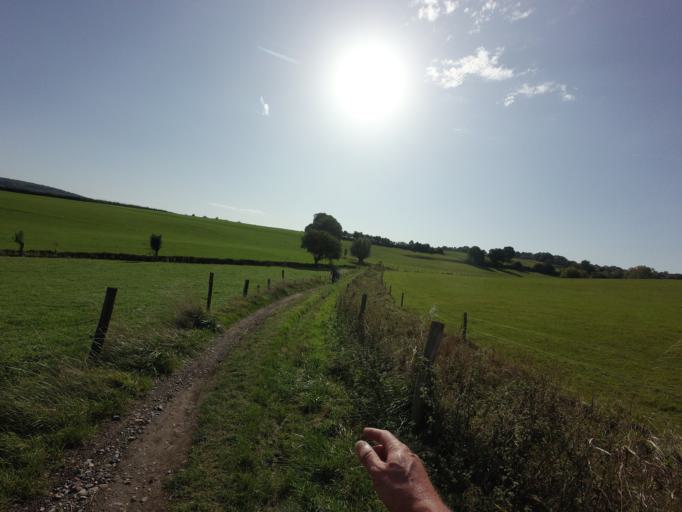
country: BE
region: Wallonia
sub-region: Province de Liege
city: Plombieres
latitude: 50.7827
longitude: 5.9068
